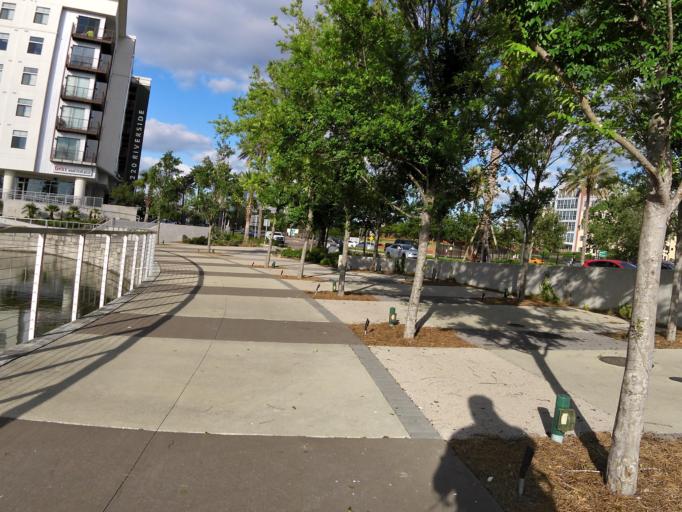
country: US
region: Florida
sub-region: Duval County
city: Jacksonville
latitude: 30.3218
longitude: -81.6740
